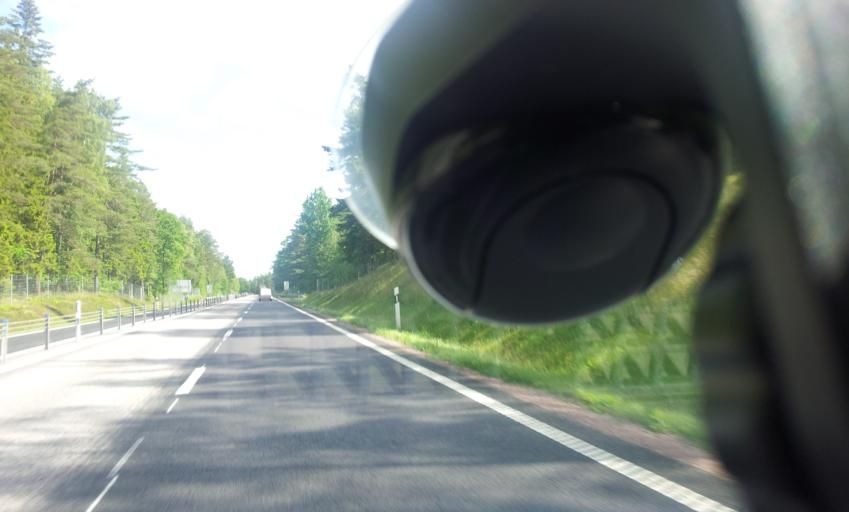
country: SE
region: Kalmar
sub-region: Monsteras Kommun
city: Timmernabben
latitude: 56.8621
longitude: 16.3797
